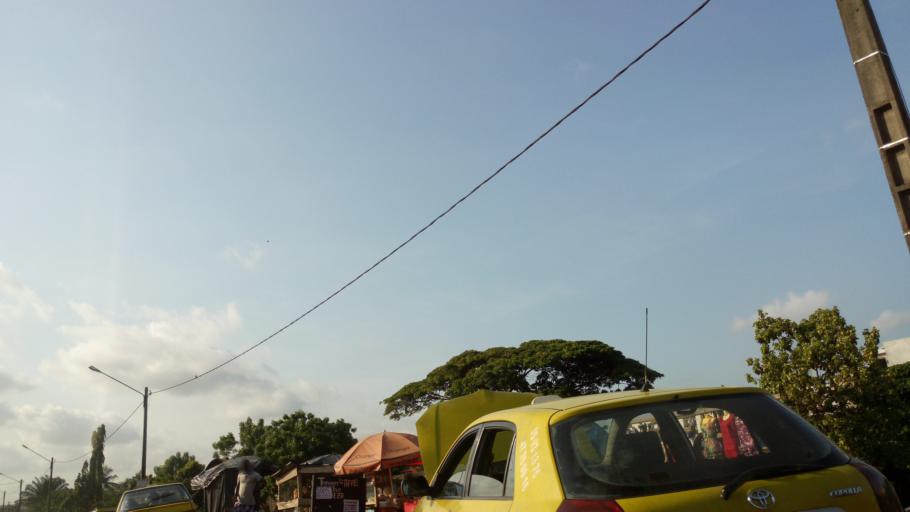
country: CI
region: Lagunes
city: Abidjan
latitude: 5.3599
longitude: -3.9617
